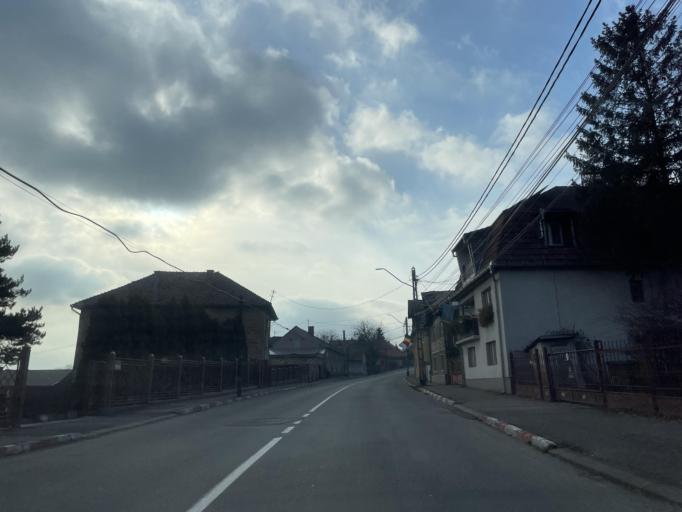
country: RO
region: Mures
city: Reghin-Sat
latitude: 46.7860
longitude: 24.7084
